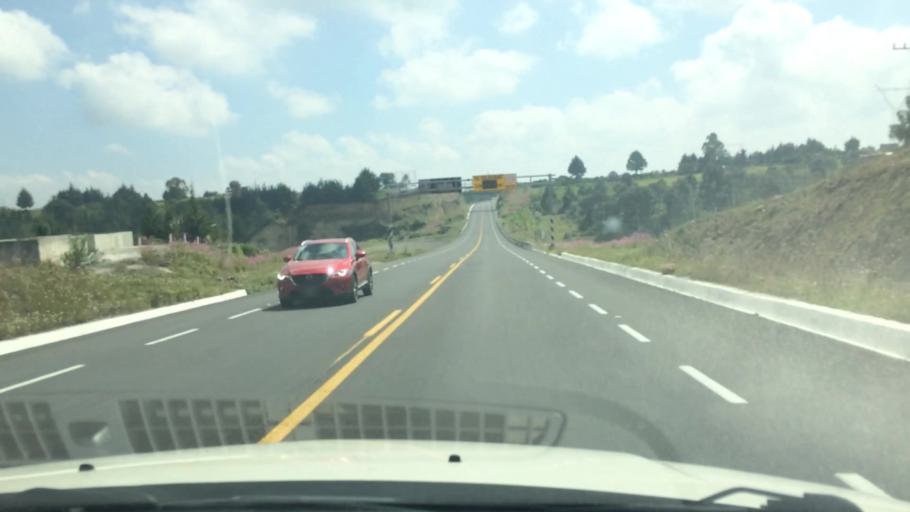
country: MX
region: Mexico
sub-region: Villa Victoria
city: Colonia Doctor Gustavo Baz
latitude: 19.3766
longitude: -99.8880
